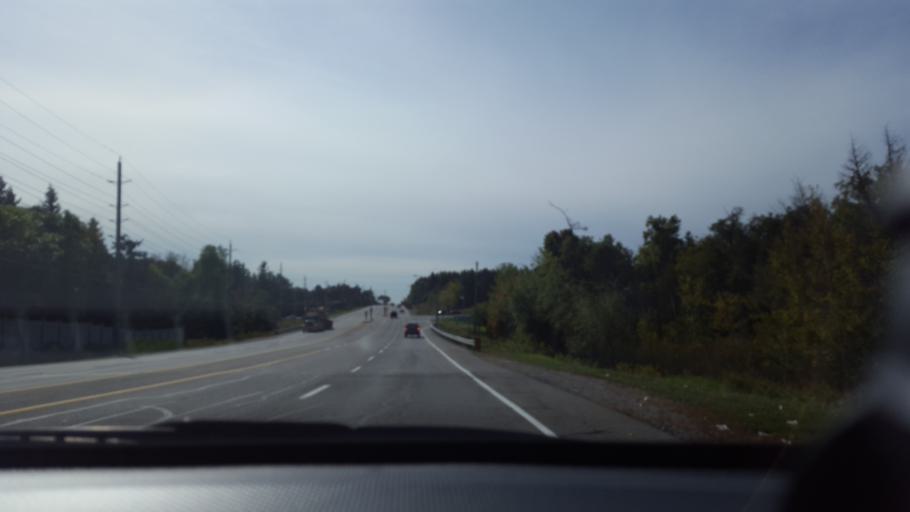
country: CA
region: Ontario
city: Newmarket
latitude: 43.9958
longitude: -79.4948
